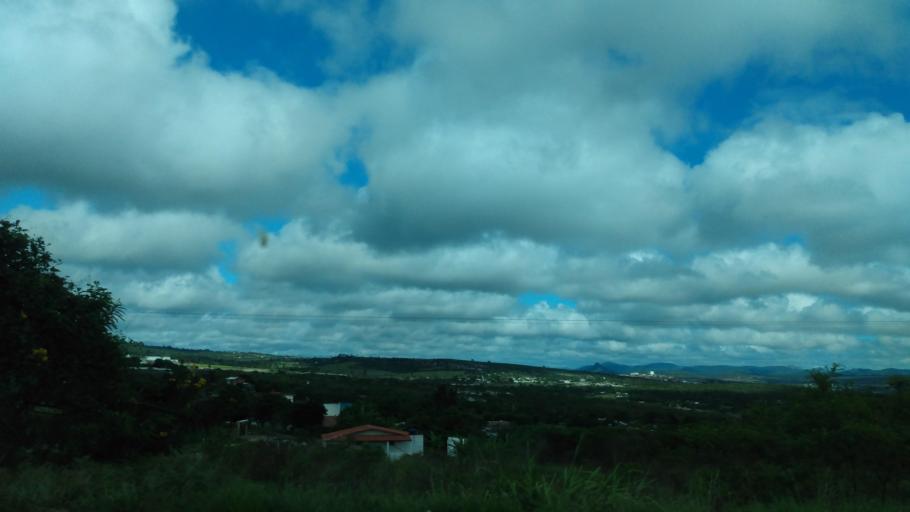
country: BR
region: Pernambuco
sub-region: Caruaru
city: Caruaru
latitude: -8.3165
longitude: -35.9915
